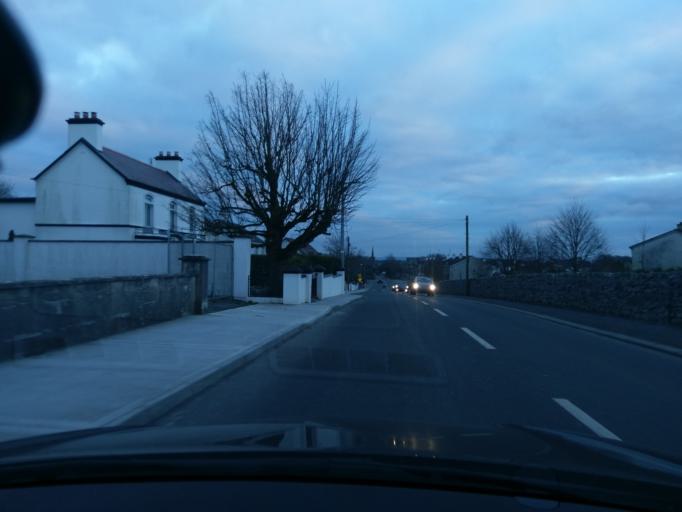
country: IE
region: Connaught
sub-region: County Galway
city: Athenry
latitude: 53.3046
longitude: -8.7503
